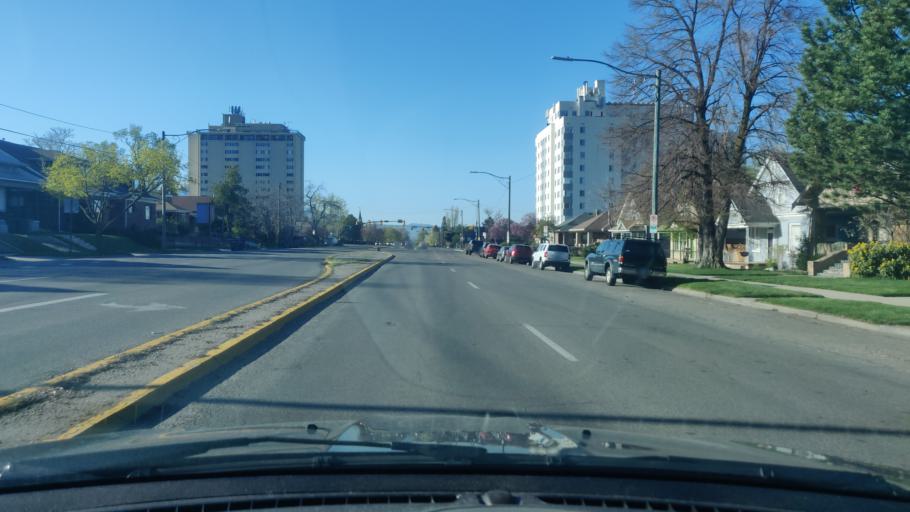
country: US
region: Utah
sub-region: Salt Lake County
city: Salt Lake City
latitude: 40.7603
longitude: -111.8539
